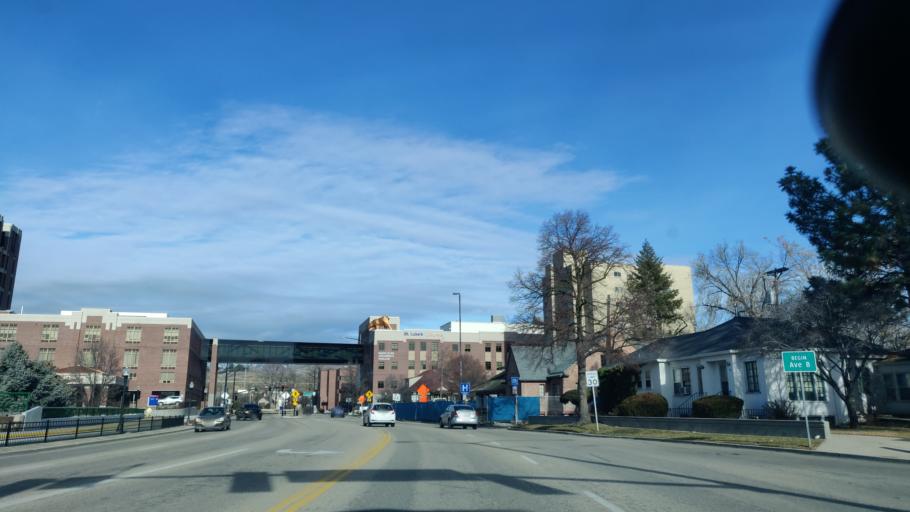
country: US
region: Idaho
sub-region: Ada County
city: Boise
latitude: 43.6112
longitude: -116.1924
